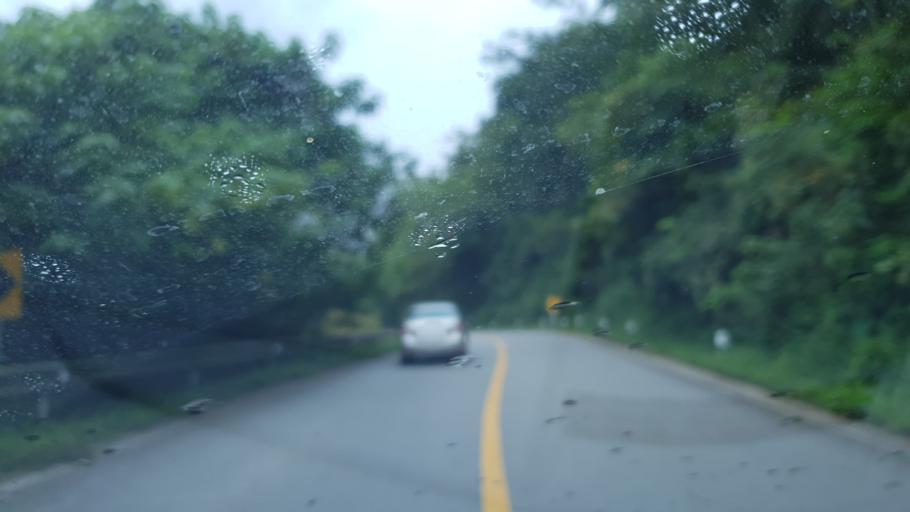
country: TH
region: Mae Hong Son
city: Khun Yuam
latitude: 18.7073
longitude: 97.9123
